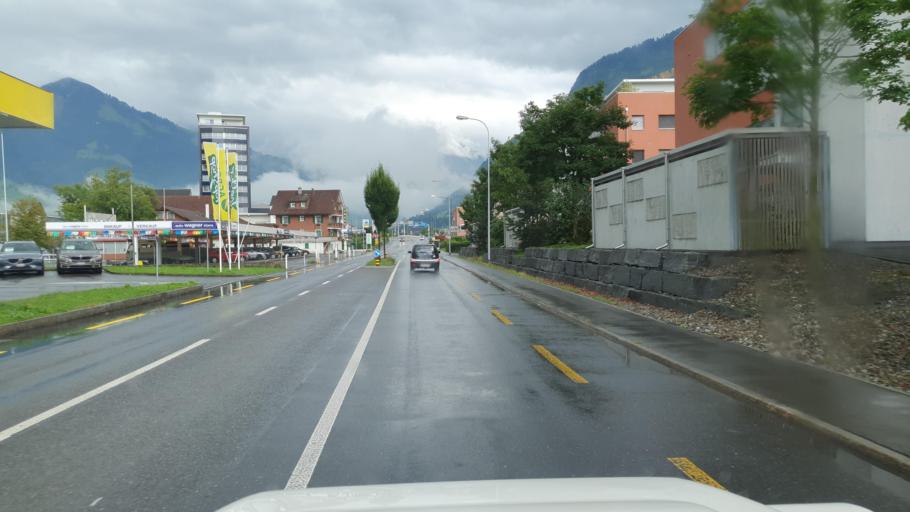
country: CH
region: Nidwalden
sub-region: Nidwalden
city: Stans
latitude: 46.9693
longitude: 8.3522
